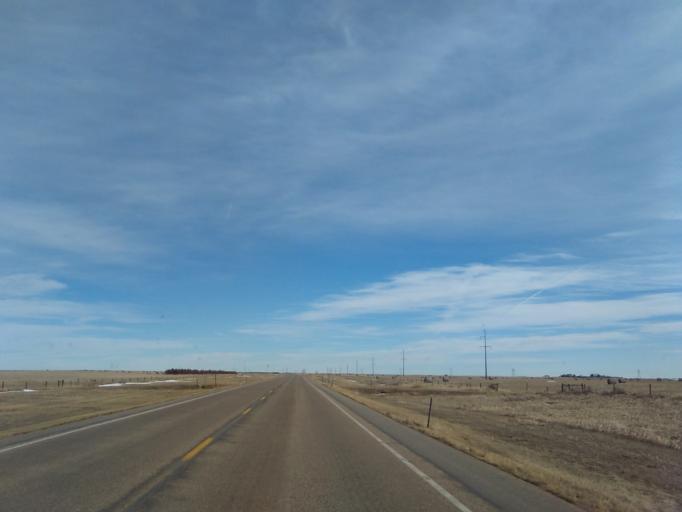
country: US
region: Wyoming
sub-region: Laramie County
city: Pine Bluffs
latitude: 41.4276
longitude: -104.3840
